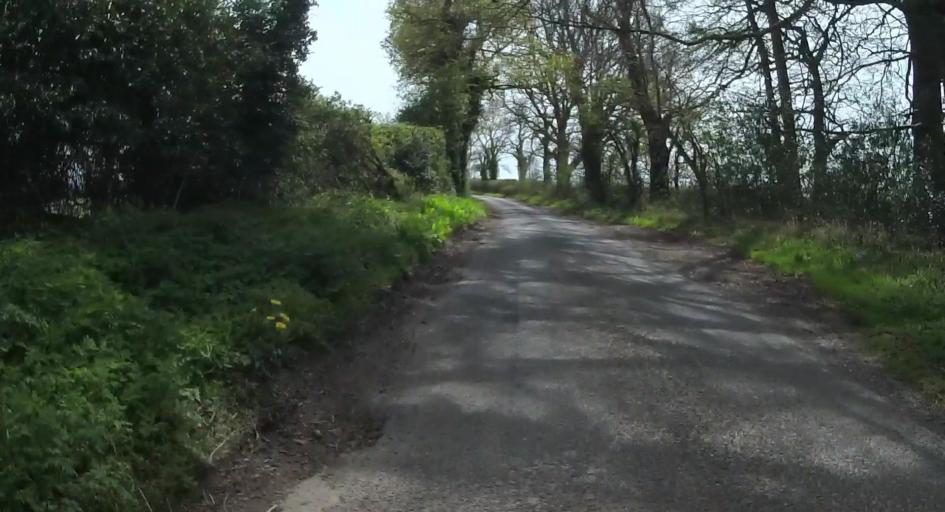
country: GB
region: England
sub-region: Hampshire
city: Alton
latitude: 51.1800
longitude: -0.9675
